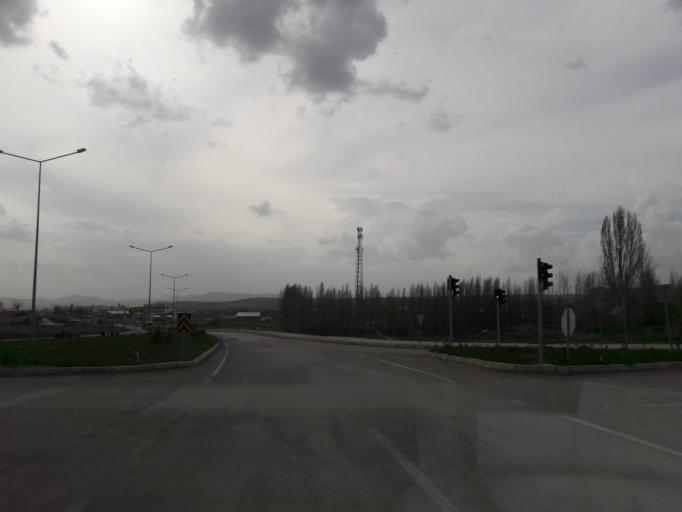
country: TR
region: Gumushane
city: Siran
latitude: 40.1793
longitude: 39.1228
